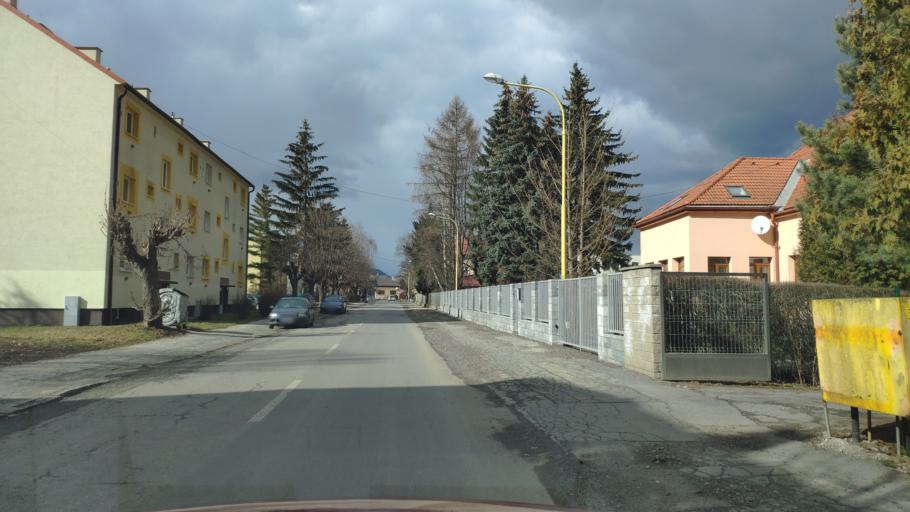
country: SK
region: Presovsky
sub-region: Okres Presov
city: Presov
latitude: 48.9938
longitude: 21.2366
